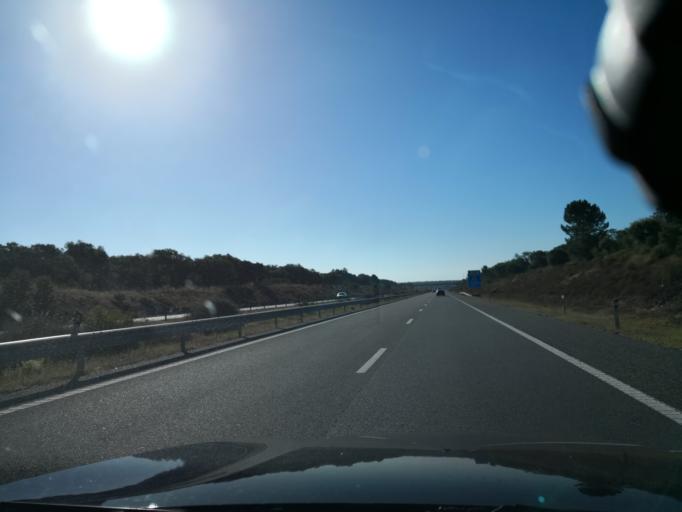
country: PT
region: Setubal
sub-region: Grandola
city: Grandola
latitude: 38.1356
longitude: -8.4379
